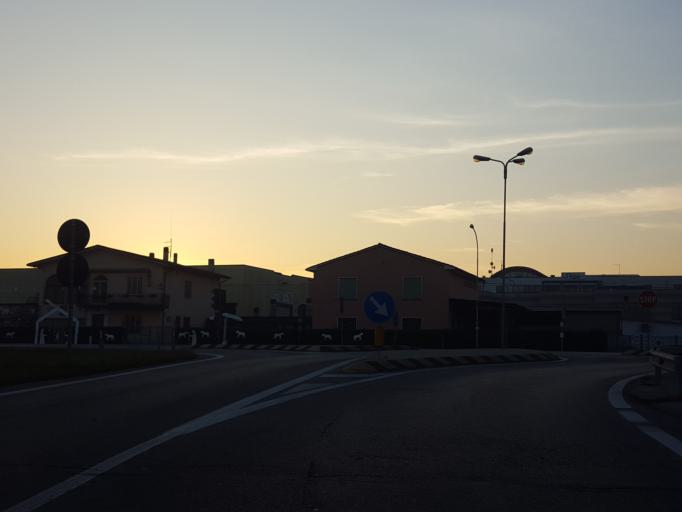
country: IT
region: Veneto
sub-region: Provincia di Vicenza
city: Quinto Vicentino
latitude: 45.5875
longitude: 11.6254
